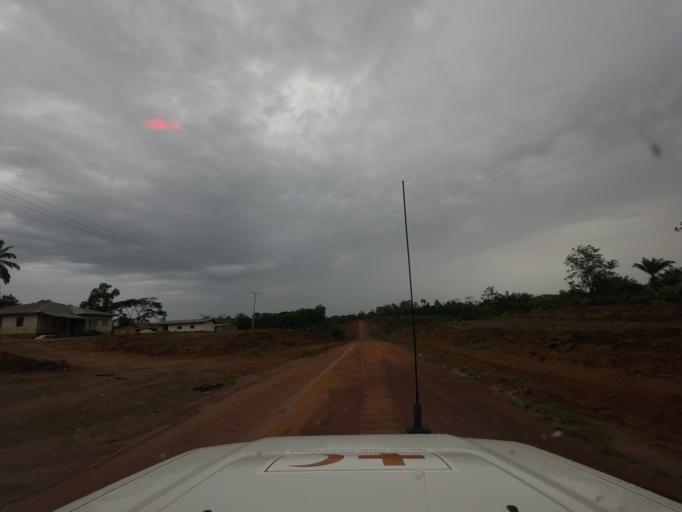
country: LR
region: Nimba
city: Sanniquellie
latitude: 7.2291
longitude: -8.9196
